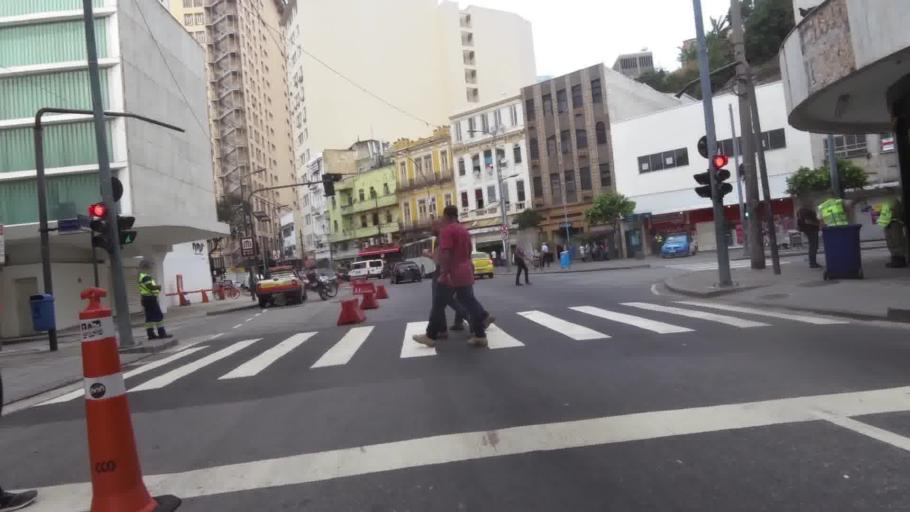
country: BR
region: Rio de Janeiro
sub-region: Rio De Janeiro
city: Rio de Janeiro
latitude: -22.8971
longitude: -43.1826
